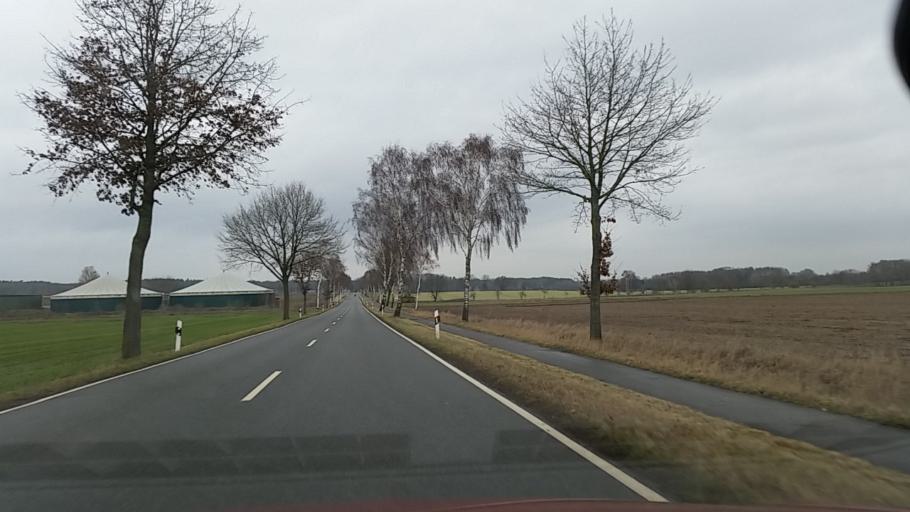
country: DE
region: Lower Saxony
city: Bispingen
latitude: 53.1186
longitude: 10.0004
